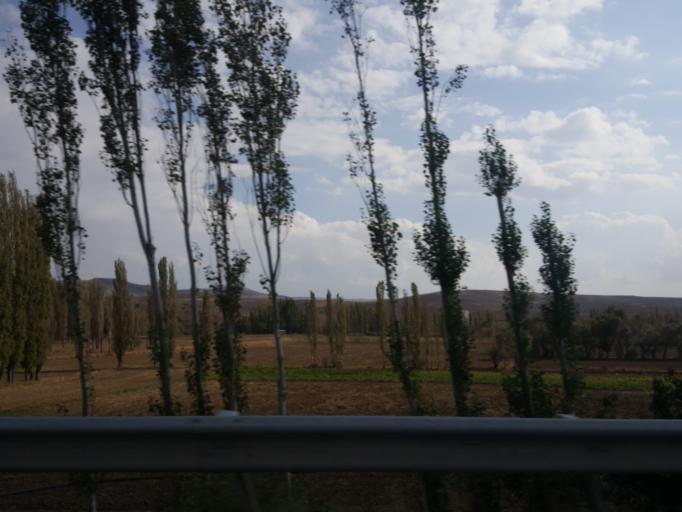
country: TR
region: Corum
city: Sungurlu
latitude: 40.2107
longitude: 34.5466
